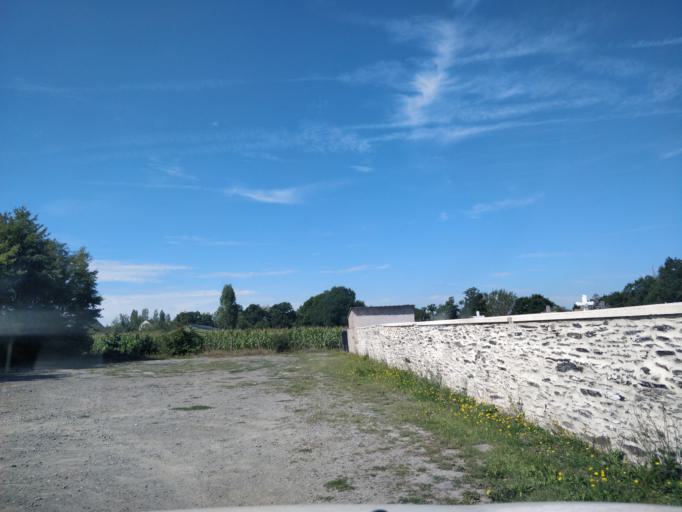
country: FR
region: Brittany
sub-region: Departement d'Ille-et-Vilaine
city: Grand-Fougeray
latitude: 47.6891
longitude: -1.7354
